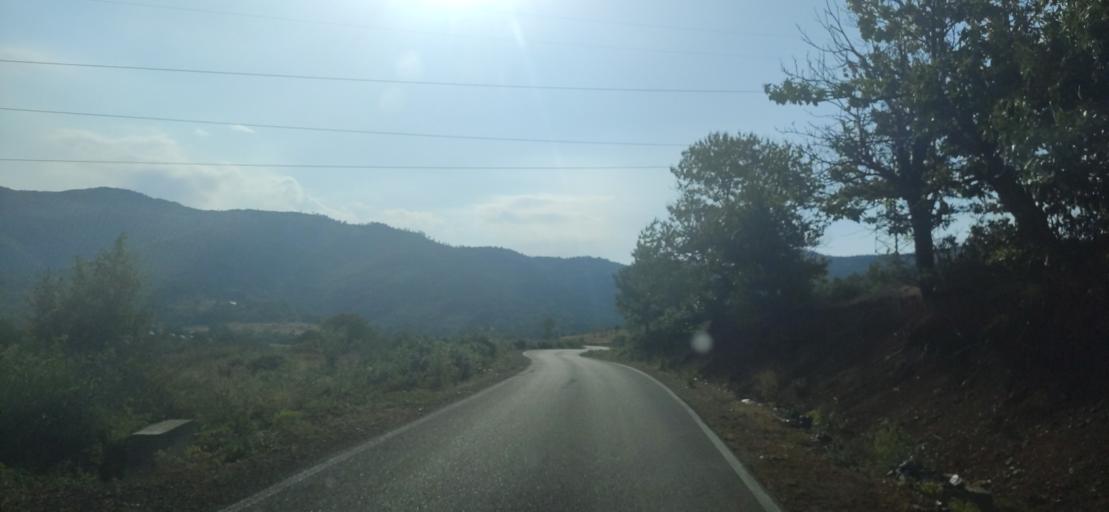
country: AL
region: Shkoder
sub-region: Rrethi i Pukes
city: Iballe
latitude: 42.1828
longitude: 19.9944
